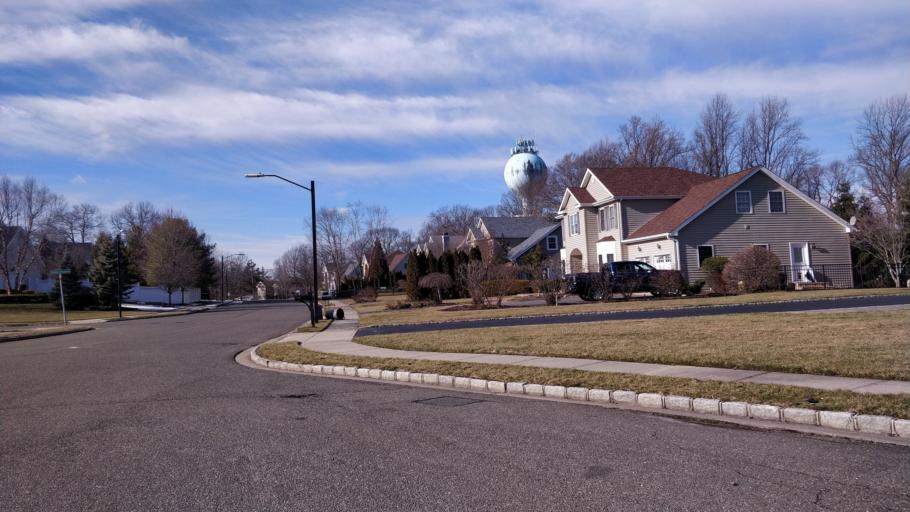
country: US
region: New York
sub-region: Nassau County
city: Oyster Bay
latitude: 40.8549
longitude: -73.5214
